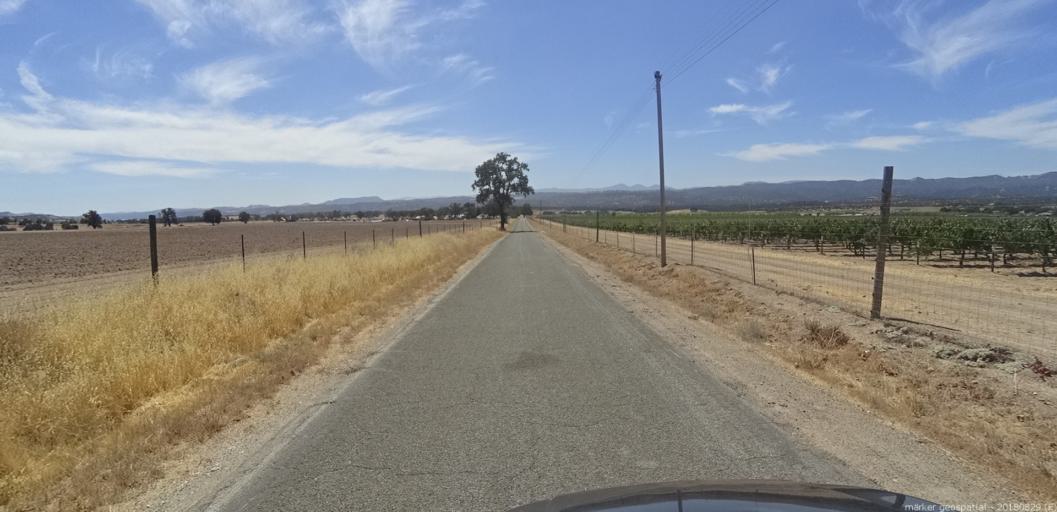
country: US
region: California
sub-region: San Luis Obispo County
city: Lake Nacimiento
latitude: 35.9213
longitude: -121.0379
